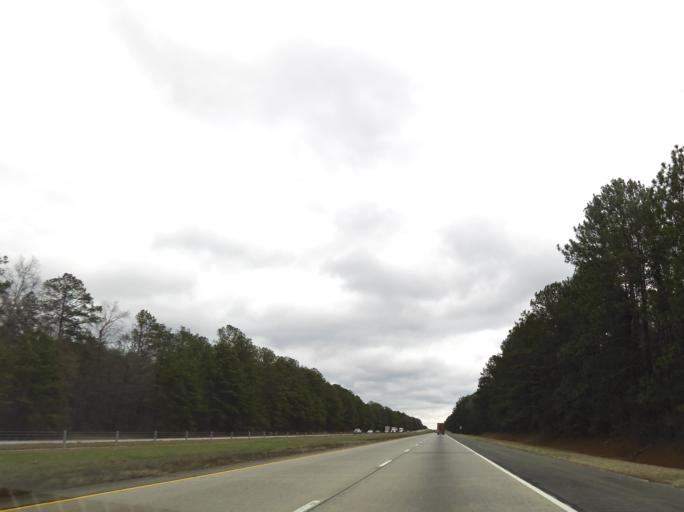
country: US
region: Georgia
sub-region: Houston County
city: Warner Robins
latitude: 32.7105
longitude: -83.5202
